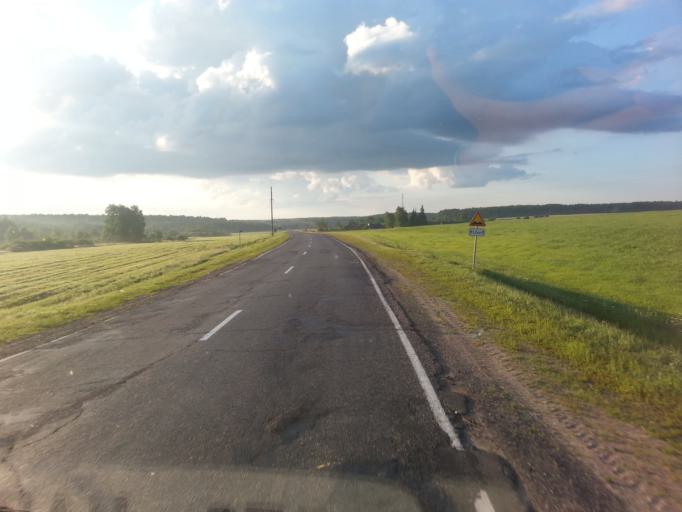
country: BY
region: Minsk
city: Il'ya
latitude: 54.4794
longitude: 27.2503
